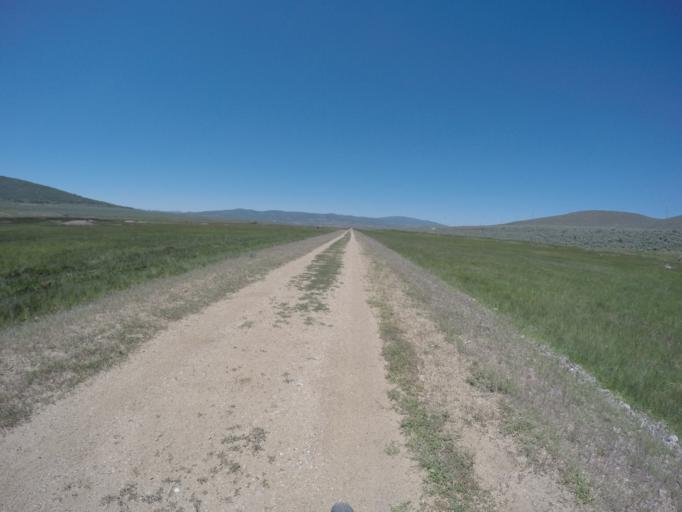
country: US
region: Utah
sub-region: Summit County
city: Park City
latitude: 40.6962
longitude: -111.4611
